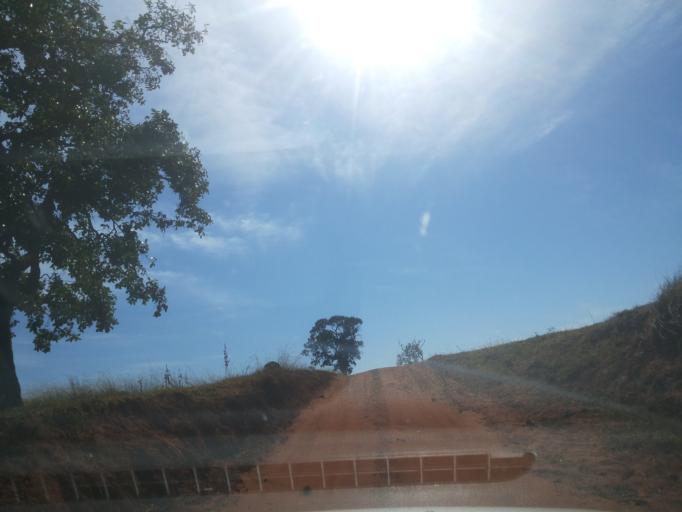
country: BR
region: Minas Gerais
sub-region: Ituiutaba
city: Ituiutaba
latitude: -19.1091
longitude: -49.4170
